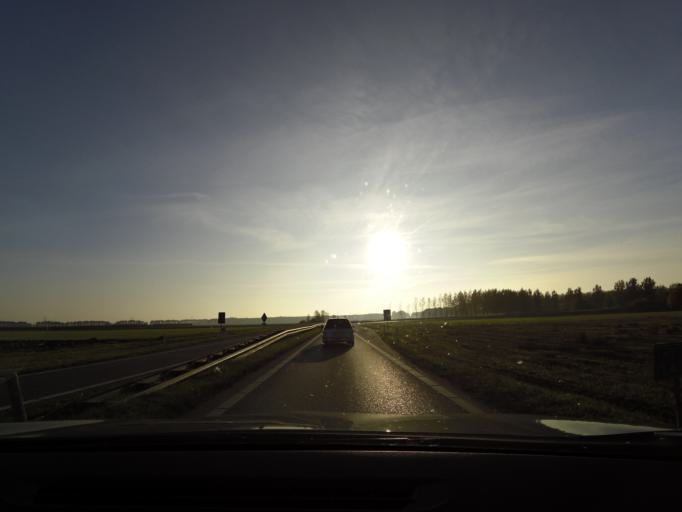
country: NL
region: South Holland
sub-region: Gemeente Strijen
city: Strijen
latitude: 51.6916
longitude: 4.6433
